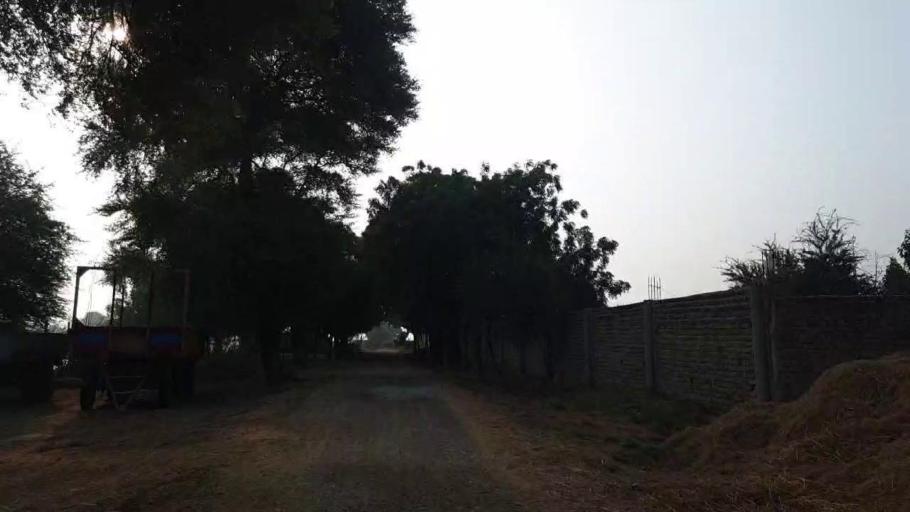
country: PK
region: Sindh
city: Tando Muhammad Khan
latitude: 25.1201
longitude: 68.5653
